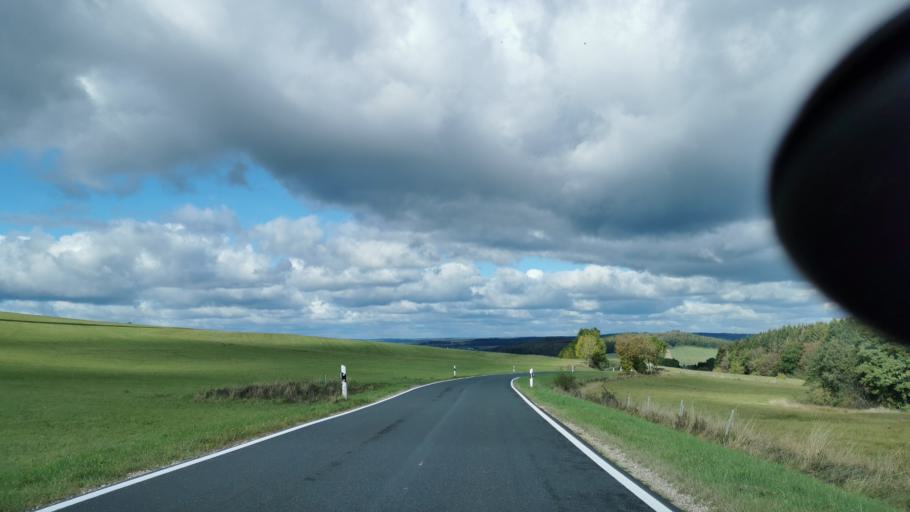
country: DE
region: Rheinland-Pfalz
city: Hohenfels-Essingen
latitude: 50.2675
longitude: 6.7409
